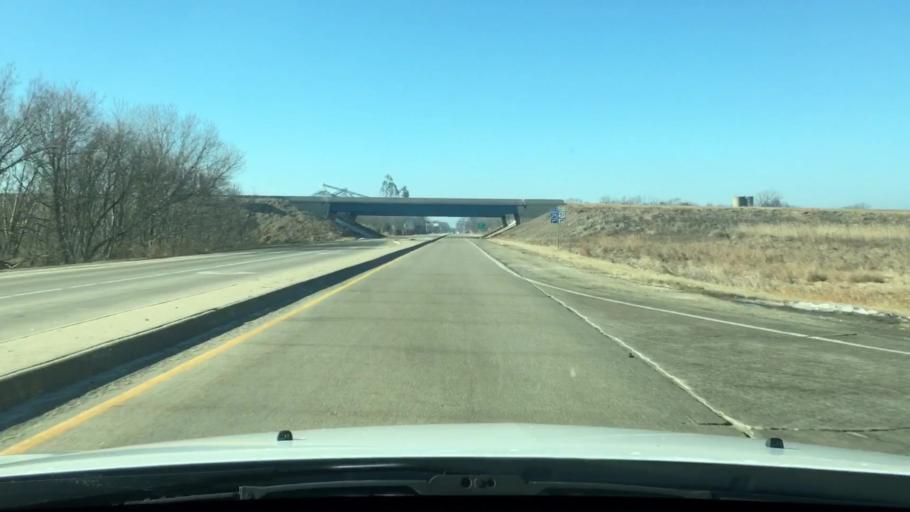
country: US
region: Illinois
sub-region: Ogle County
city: Rochelle
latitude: 41.8477
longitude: -89.0081
